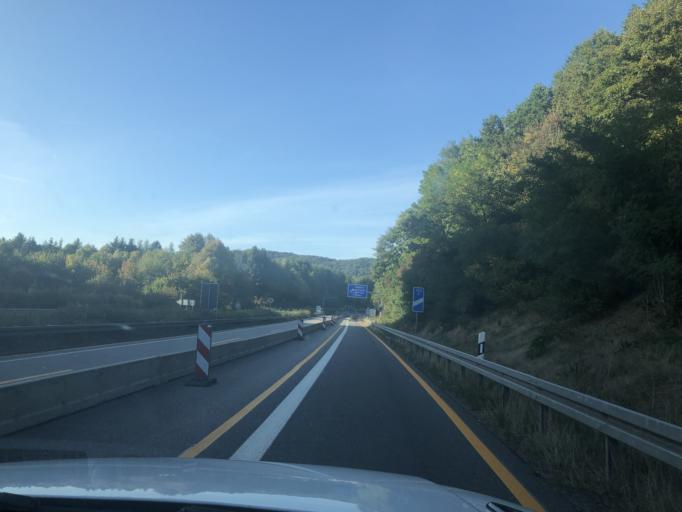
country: DE
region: Saarland
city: Tholey
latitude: 49.4865
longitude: 6.9885
